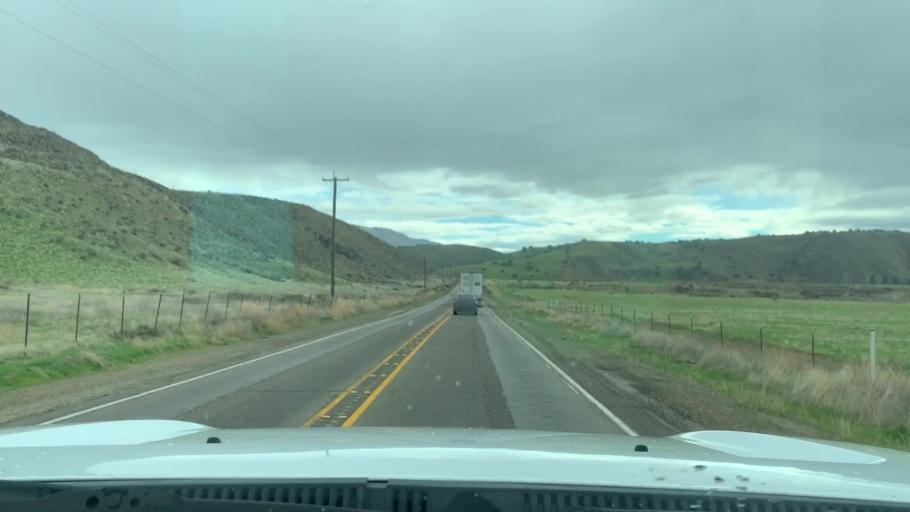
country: US
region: California
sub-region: Santa Barbara County
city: Los Olivos
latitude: 35.0595
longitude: -119.9435
